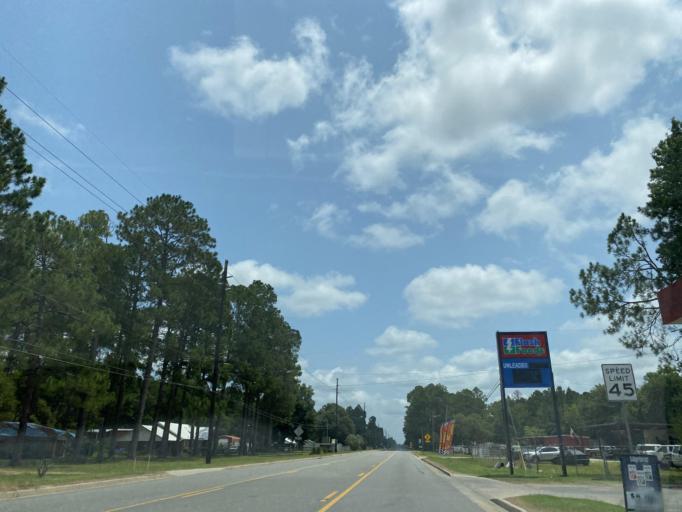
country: US
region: Georgia
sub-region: Jeff Davis County
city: Hazlehurst
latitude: 31.8462
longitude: -82.5875
